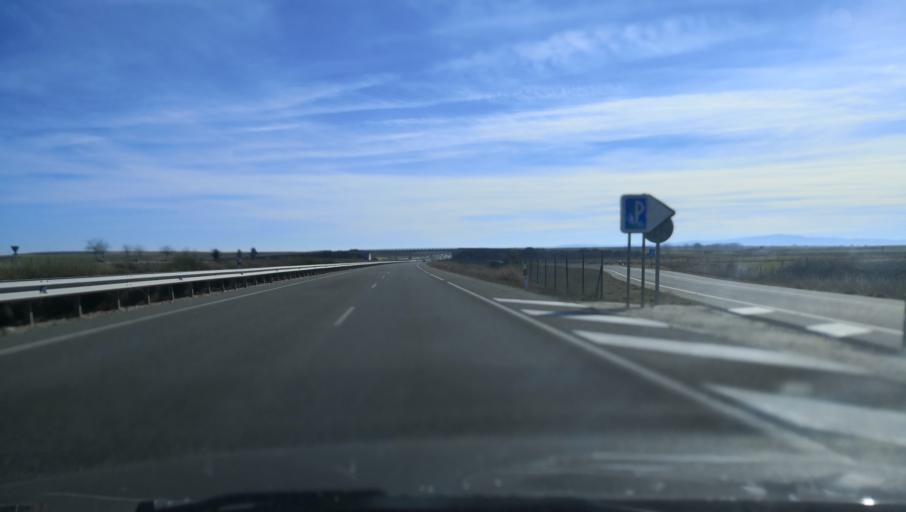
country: ES
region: Castille and Leon
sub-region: Provincia de Salamanca
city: Cantaracillo
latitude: 40.8899
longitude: -5.1530
